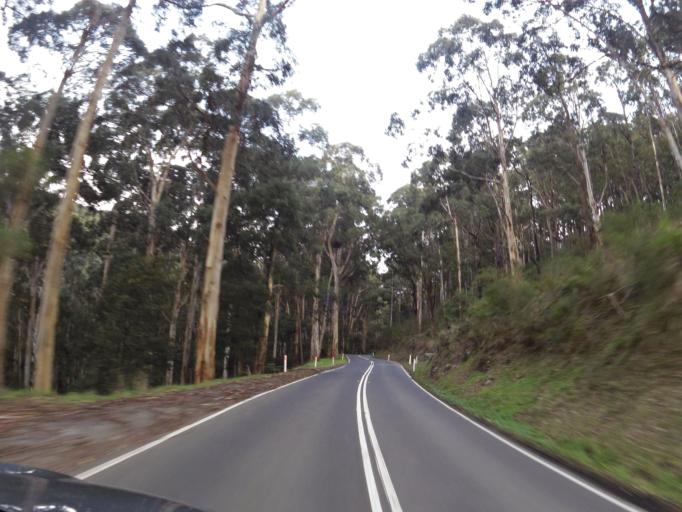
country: AU
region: Victoria
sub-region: Yarra Ranges
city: Ferny Creek
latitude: -37.8629
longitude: 145.3427
